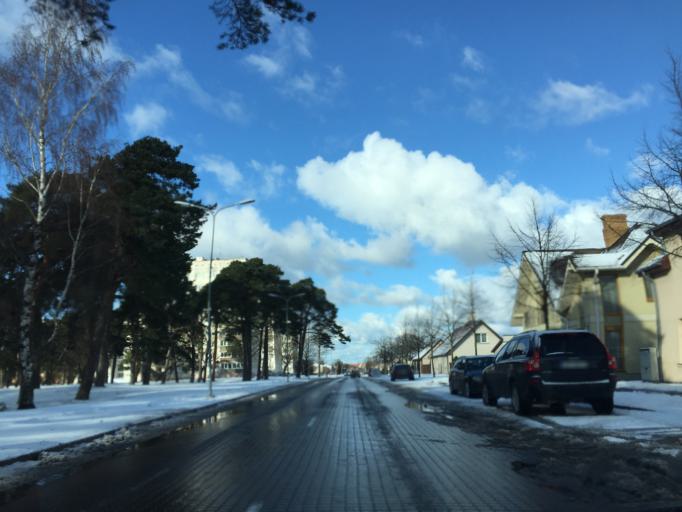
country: LV
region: Ventspils
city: Ventspils
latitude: 57.3795
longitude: 21.5524
